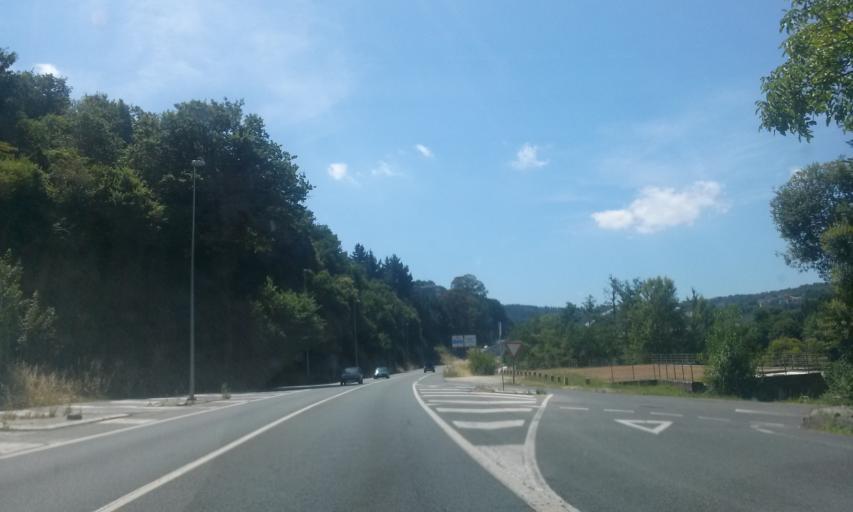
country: ES
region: Galicia
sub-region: Provincia de Lugo
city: Lugo
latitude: 43.0010
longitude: -7.5603
